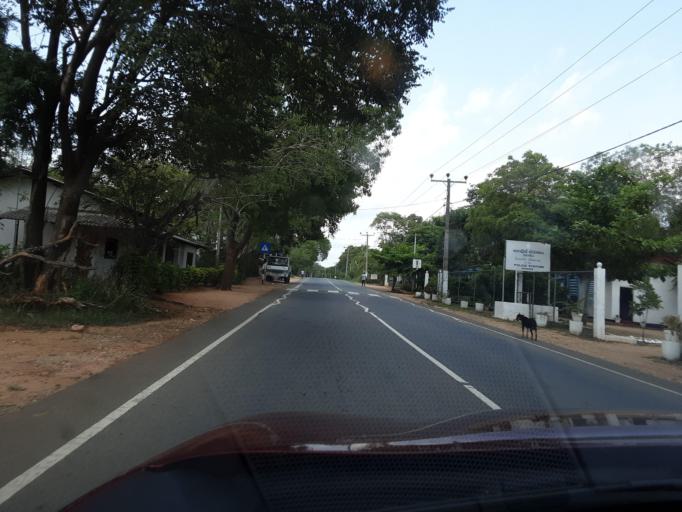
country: LK
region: Uva
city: Haputale
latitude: 6.5330
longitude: 81.1317
